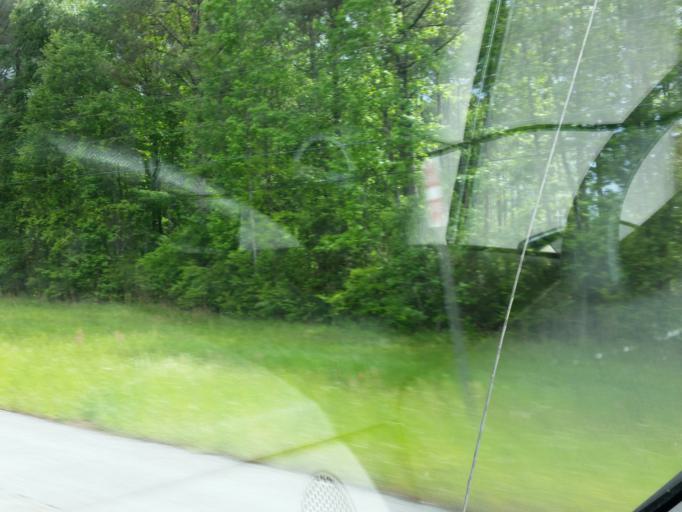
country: US
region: Georgia
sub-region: Lamar County
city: Barnesville
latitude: 33.1304
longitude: -84.2259
